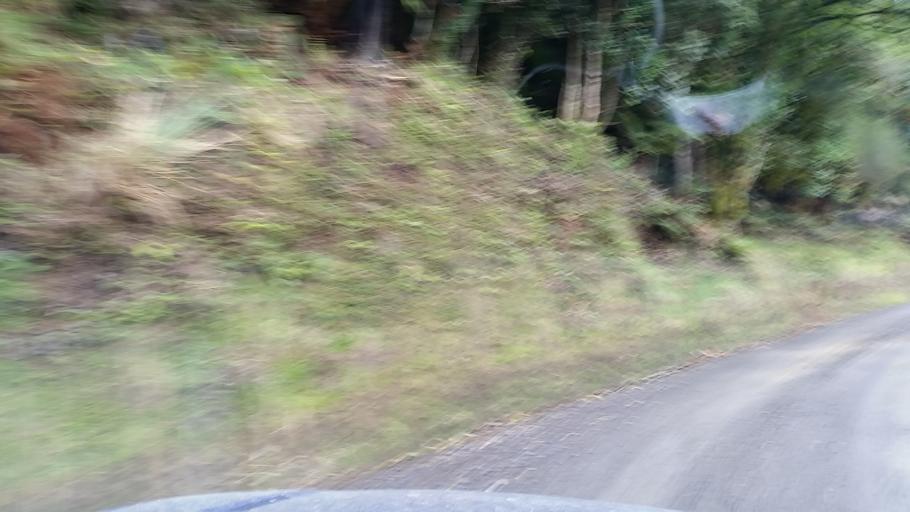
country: NZ
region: Taranaki
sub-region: South Taranaki District
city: Eltham
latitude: -39.1700
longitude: 174.6261
